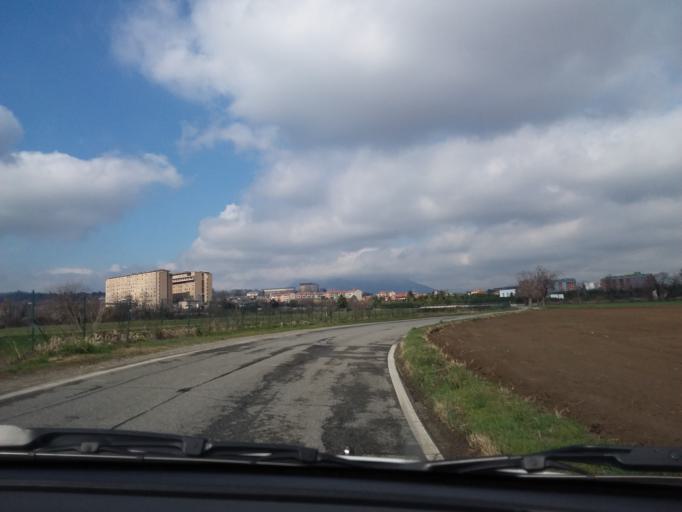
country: IT
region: Piedmont
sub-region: Provincia di Torino
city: Tetti Neirotti
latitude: 45.0569
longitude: 7.5284
